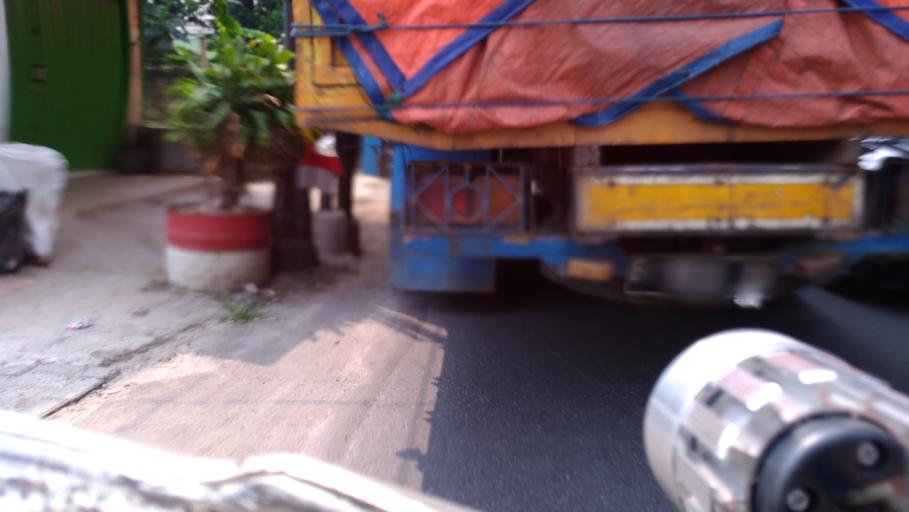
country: ID
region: West Java
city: Depok
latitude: -6.3397
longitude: 106.8804
